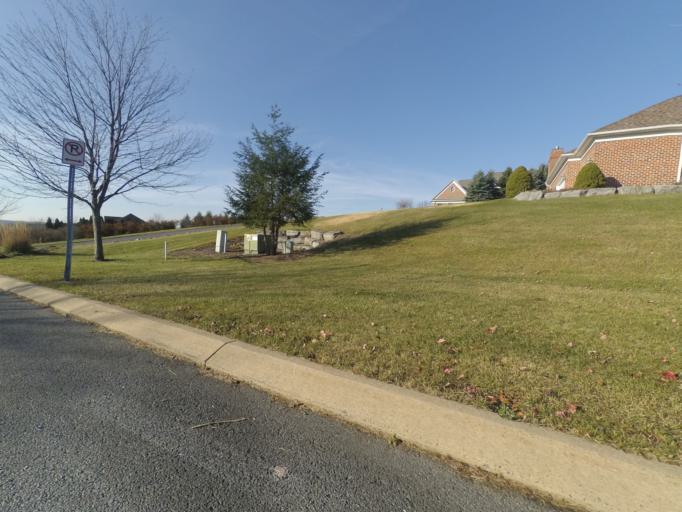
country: US
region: Pennsylvania
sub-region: Centre County
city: Lemont
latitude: 40.7950
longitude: -77.8233
